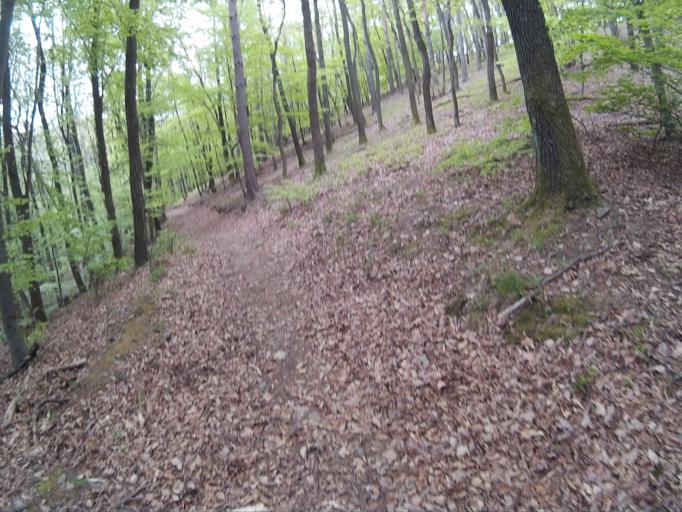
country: HU
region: Vas
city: Koszeg
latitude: 47.3524
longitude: 16.4946
